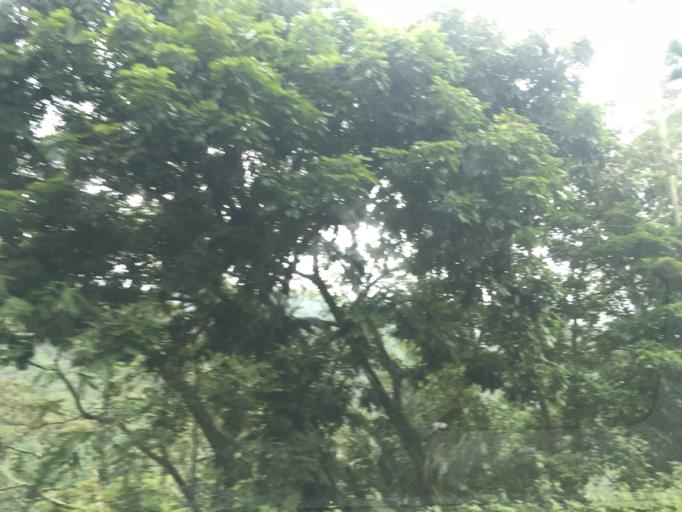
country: TW
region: Taiwan
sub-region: Yunlin
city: Douliu
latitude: 23.5721
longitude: 120.6452
